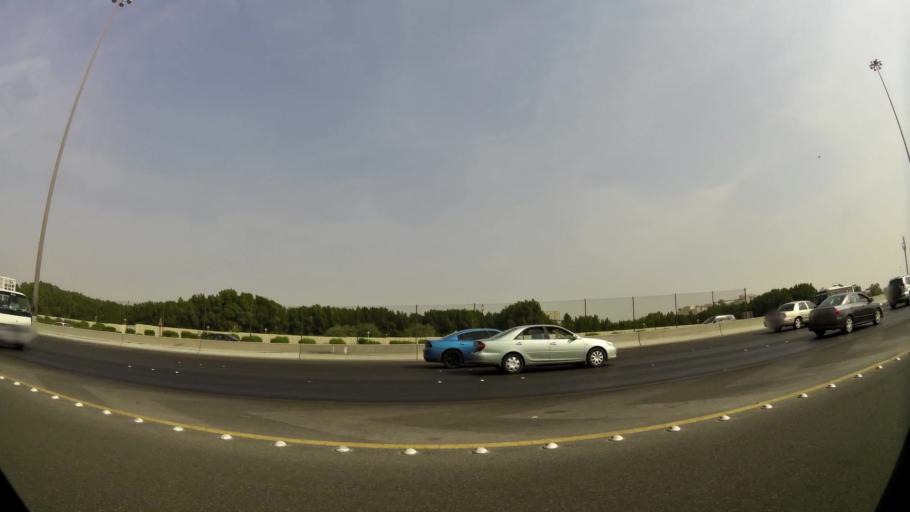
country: KW
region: Al Asimah
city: Ar Rabiyah
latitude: 29.2927
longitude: 47.9470
